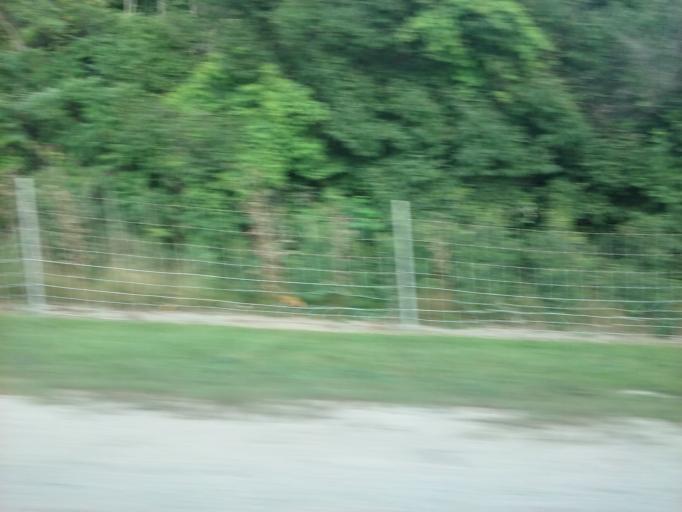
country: US
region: Ohio
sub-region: Wood County
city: Bowling Green
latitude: 41.3130
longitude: -83.6503
